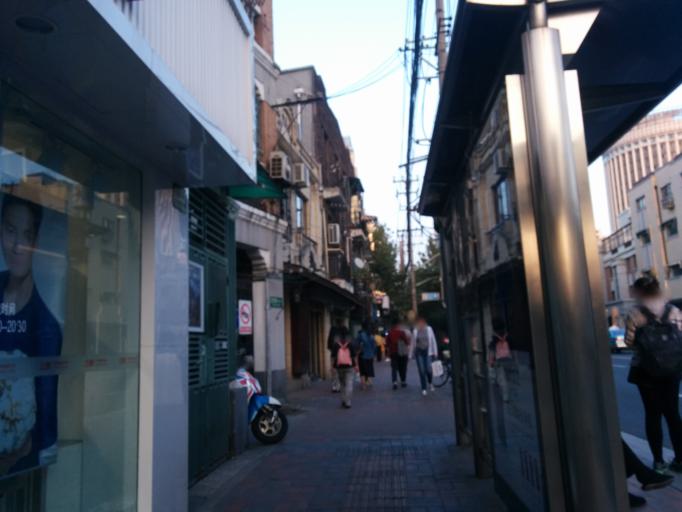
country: CN
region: Shanghai Shi
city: Shanghai
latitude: 31.2156
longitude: 121.4470
